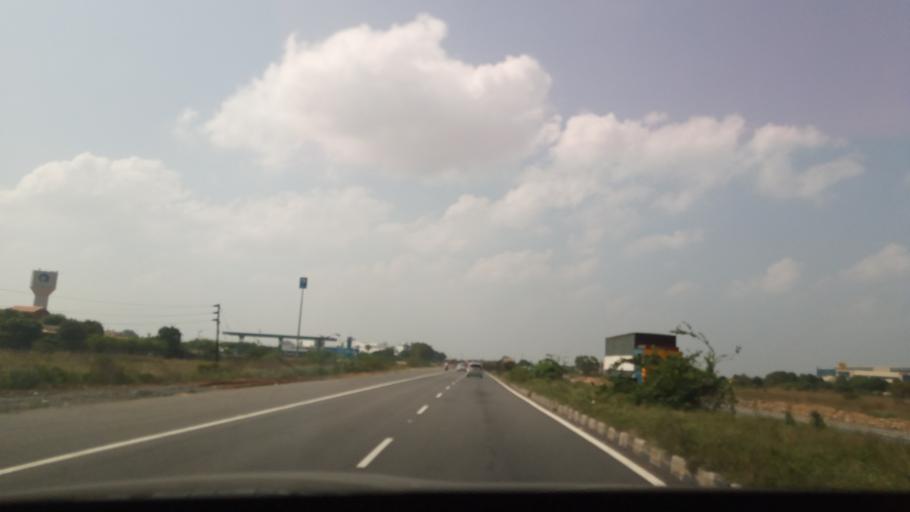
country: IN
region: Tamil Nadu
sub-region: Kancheepuram
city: Wallajahbad
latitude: 12.8987
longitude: 79.8078
